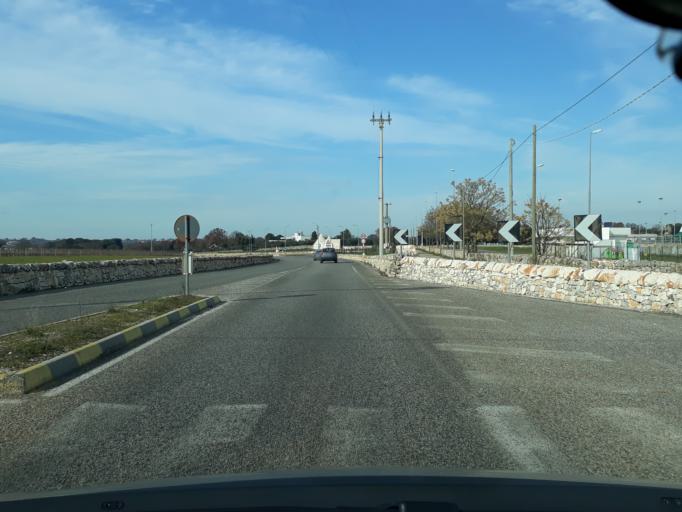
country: IT
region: Apulia
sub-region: Provincia di Bari
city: Locorotondo
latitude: 40.7560
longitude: 17.3433
